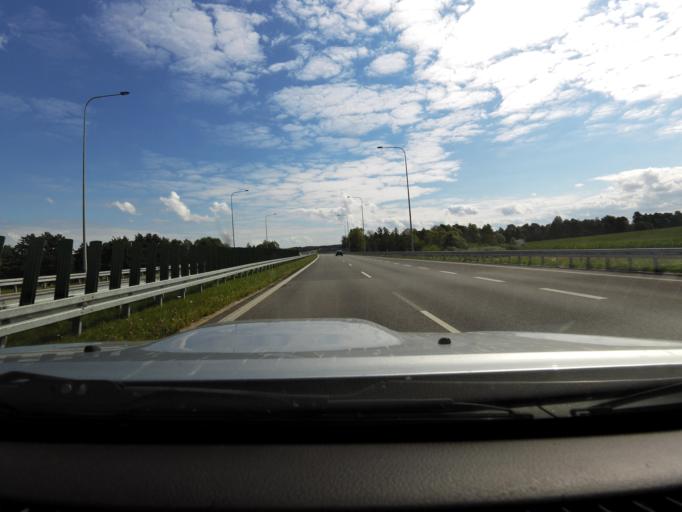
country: PL
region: Warmian-Masurian Voivodeship
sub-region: Powiat ostrodzki
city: Milomlyn
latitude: 53.7758
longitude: 19.8255
